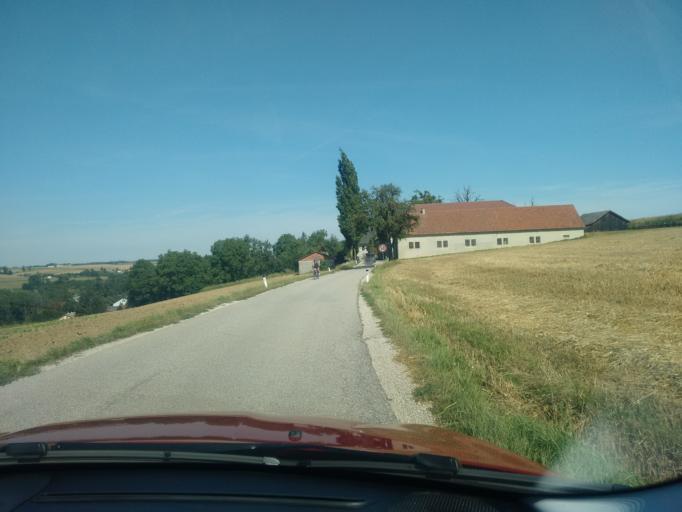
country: AT
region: Upper Austria
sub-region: Wels-Land
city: Steinhaus
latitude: 48.1097
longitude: 14.0246
